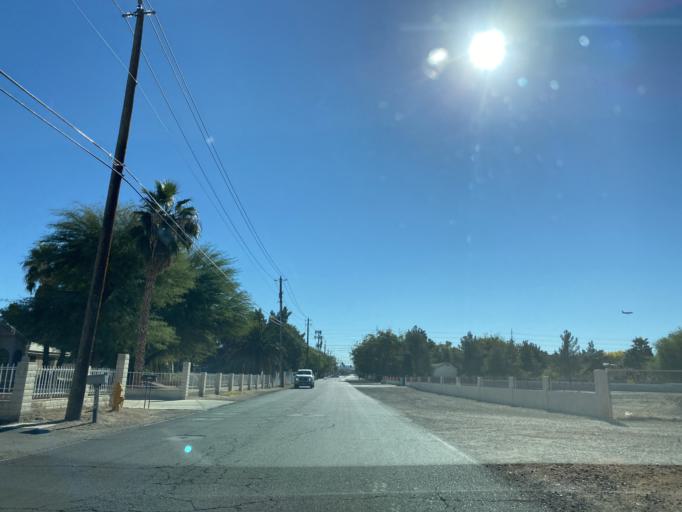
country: US
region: Nevada
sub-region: Clark County
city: Whitney
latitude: 36.0881
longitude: -115.0868
